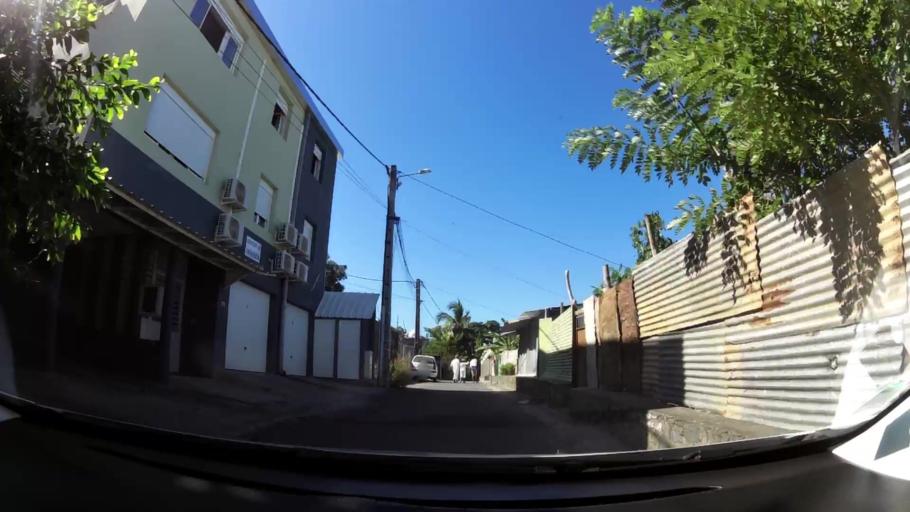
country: YT
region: Pamandzi
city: Pamandzi
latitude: -12.7833
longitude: 45.2782
